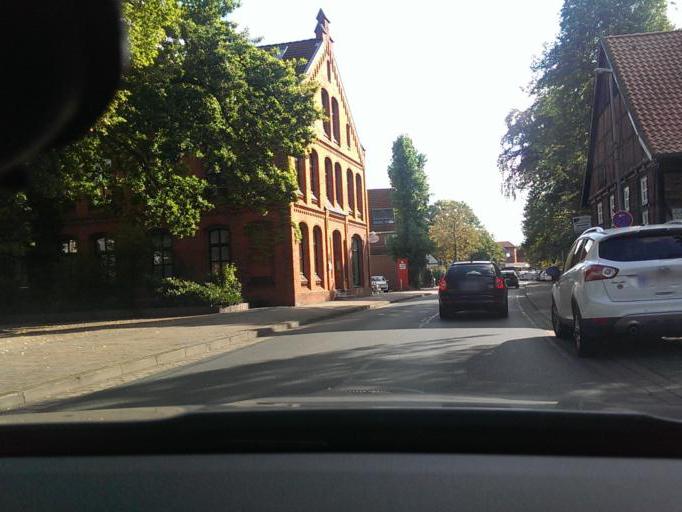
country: DE
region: Lower Saxony
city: Isernhagen Farster Bauerschaft
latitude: 52.4919
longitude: 9.8546
